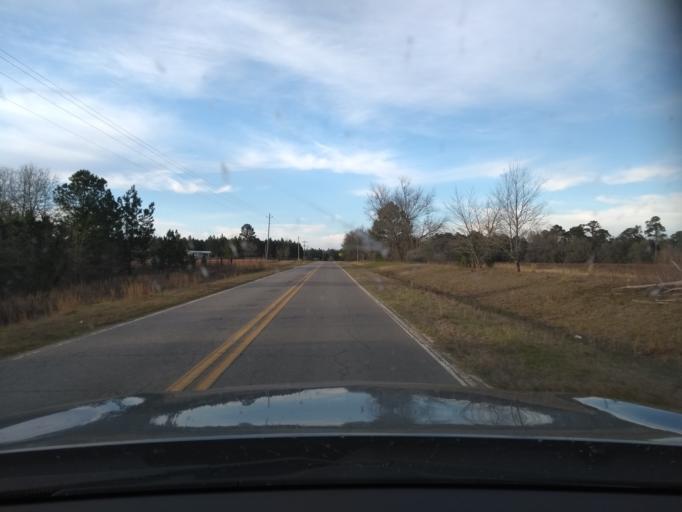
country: US
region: Georgia
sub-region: Evans County
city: Claxton
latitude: 32.2305
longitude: -81.7707
